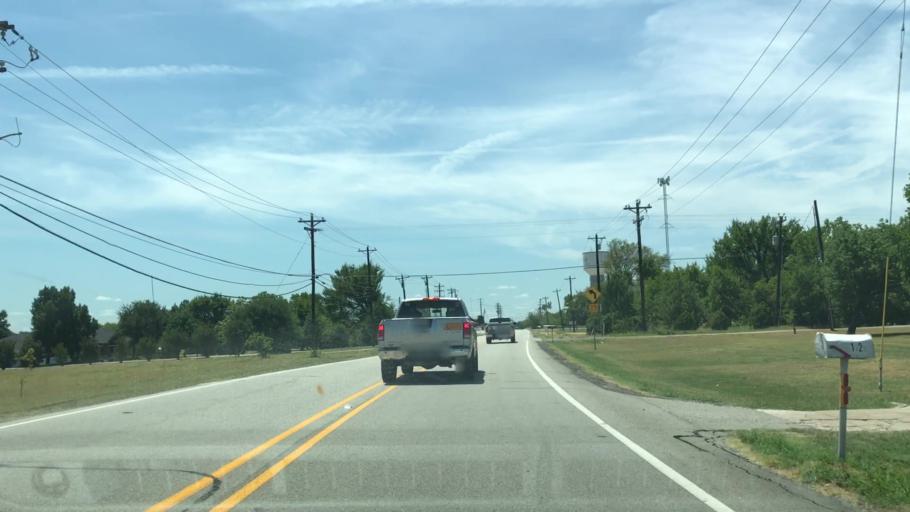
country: US
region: Texas
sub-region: Collin County
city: Saint Paul
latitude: 33.0323
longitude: -96.5470
